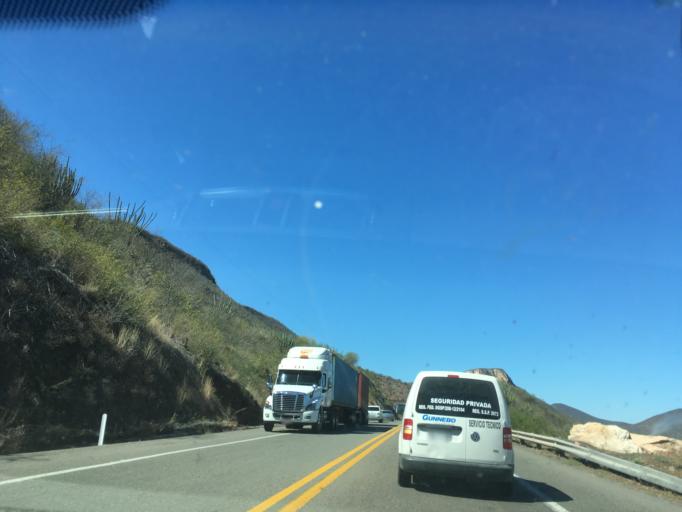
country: MX
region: Michoacan
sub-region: Arteaga
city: Las Canas
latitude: 18.4366
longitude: -101.9254
